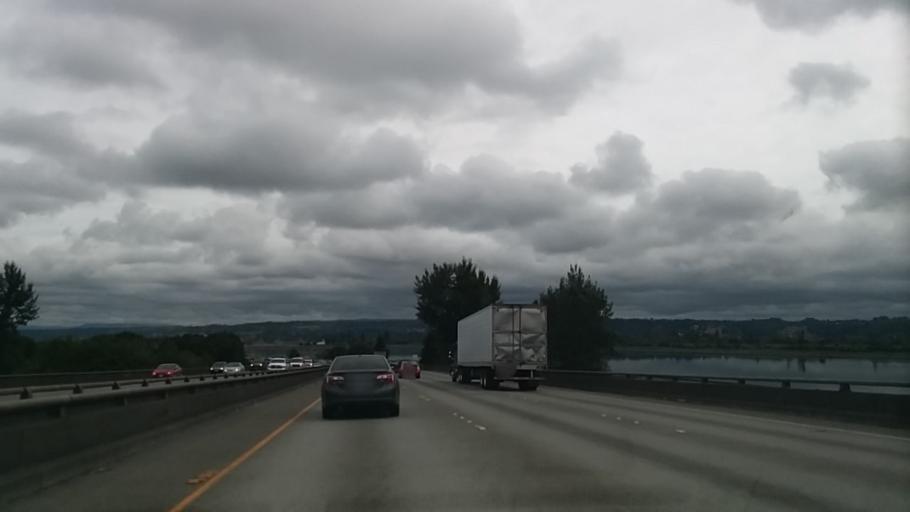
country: US
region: Washington
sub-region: Snohomish County
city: Everett
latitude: 47.9941
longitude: -122.1785
